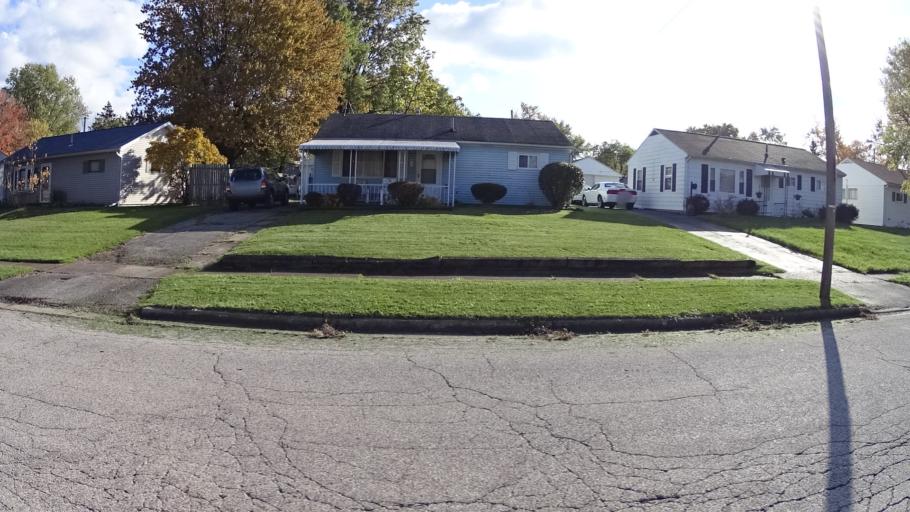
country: US
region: Ohio
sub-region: Lorain County
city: Sheffield
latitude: 41.4355
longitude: -82.1066
